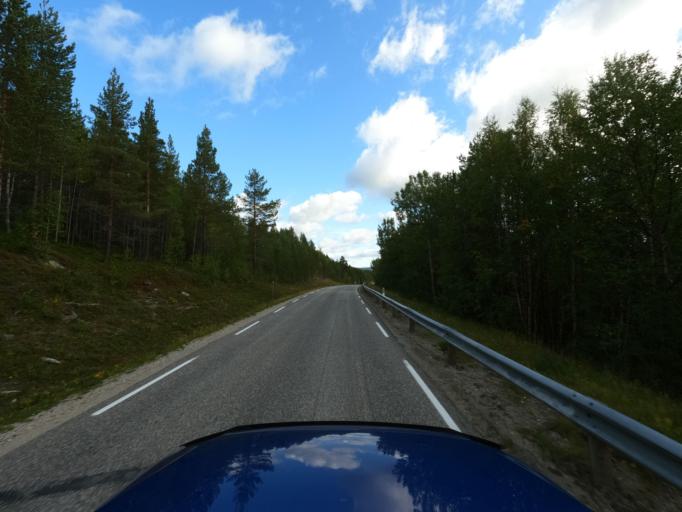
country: NO
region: Finnmark Fylke
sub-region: Karasjok
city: Karasjohka
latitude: 69.4536
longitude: 25.3802
